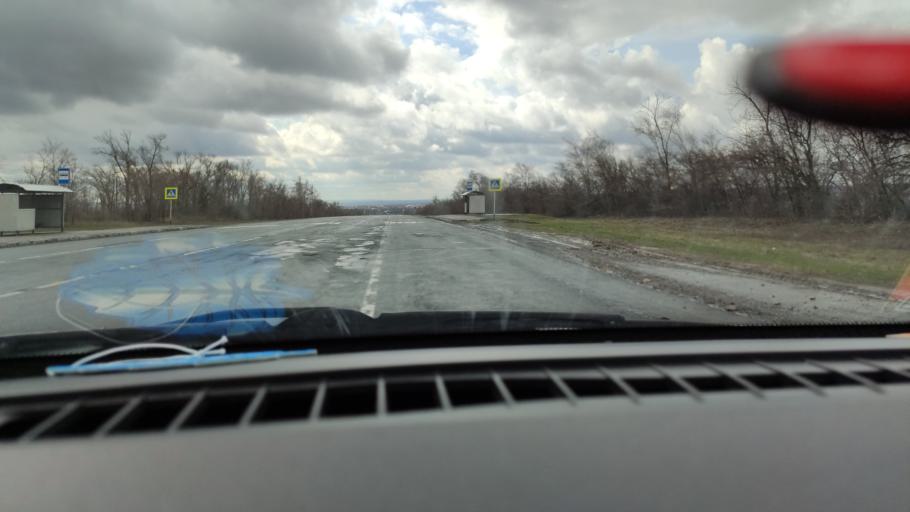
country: RU
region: Samara
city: Yelkhovka
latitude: 53.9148
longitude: 50.2645
